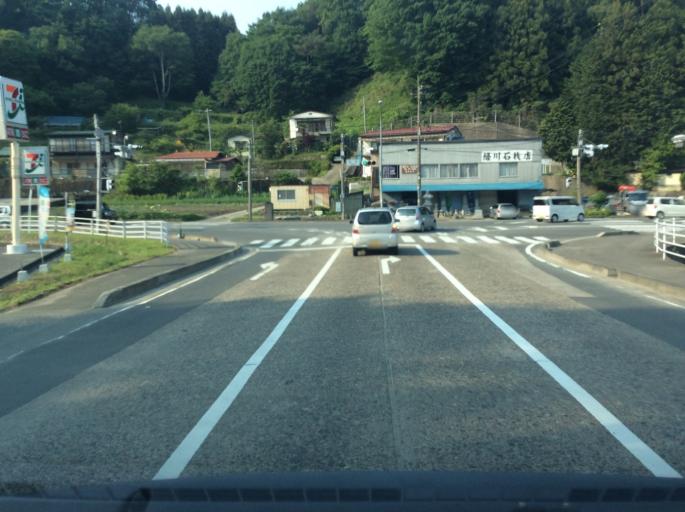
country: JP
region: Fukushima
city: Sukagawa
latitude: 37.1404
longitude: 140.2264
